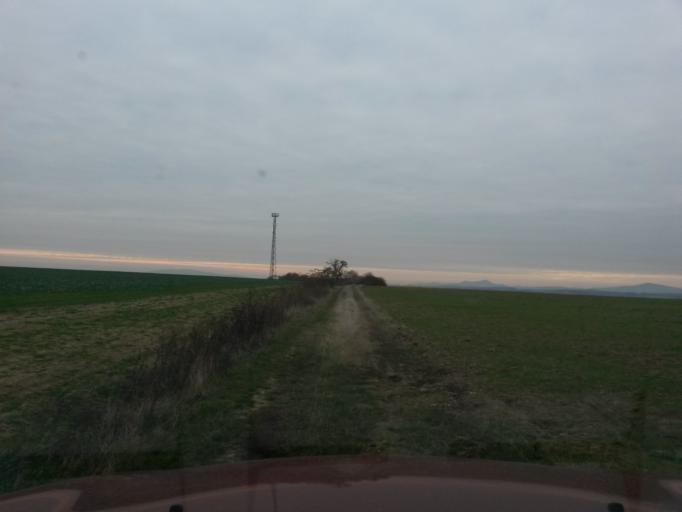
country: SK
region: Kosicky
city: Secovce
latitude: 48.6416
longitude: 21.6268
